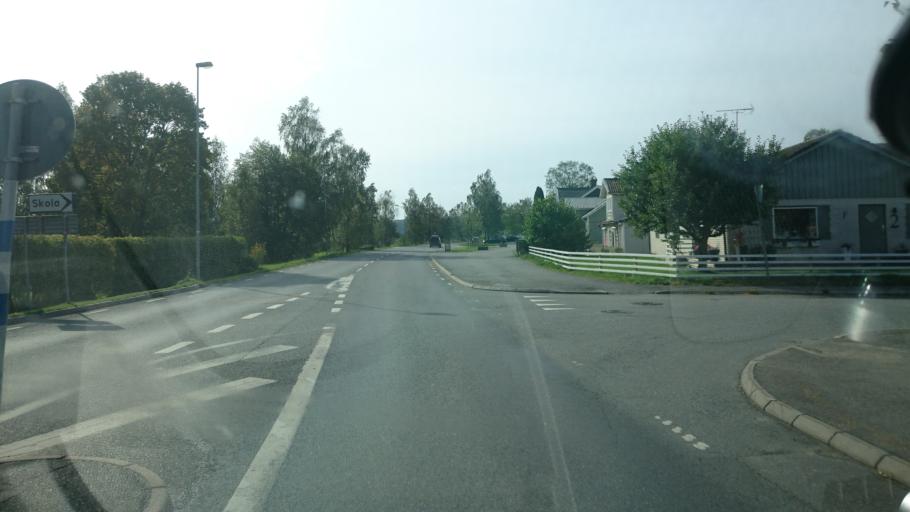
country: SE
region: Vaestra Goetaland
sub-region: Alingsas Kommun
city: Sollebrunn
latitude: 58.1183
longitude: 12.5332
